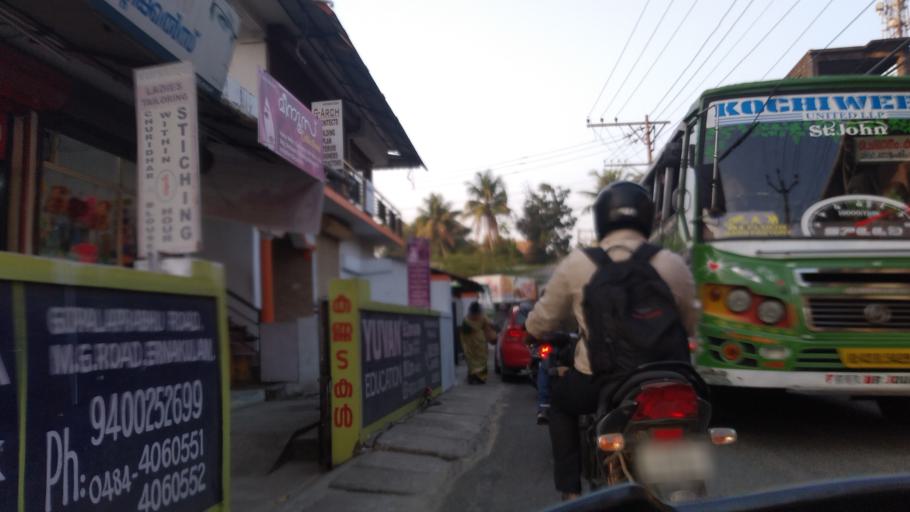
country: IN
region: Kerala
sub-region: Ernakulam
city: Elur
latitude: 10.0373
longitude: 76.2753
